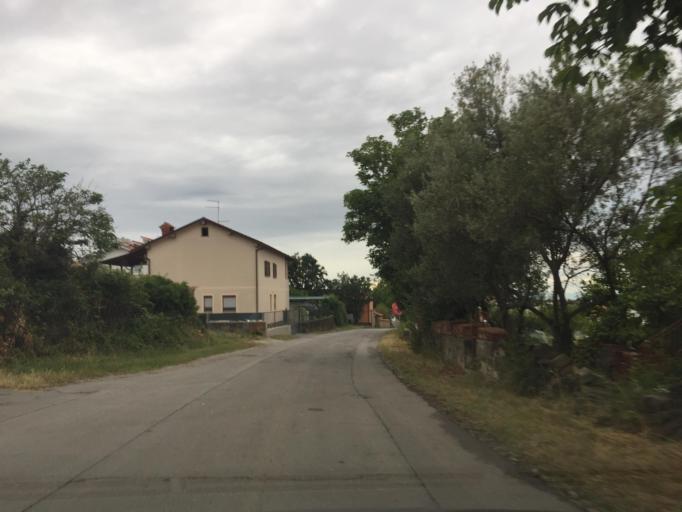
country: SI
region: Koper-Capodistria
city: Hrvatini
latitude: 45.5805
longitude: 13.7681
